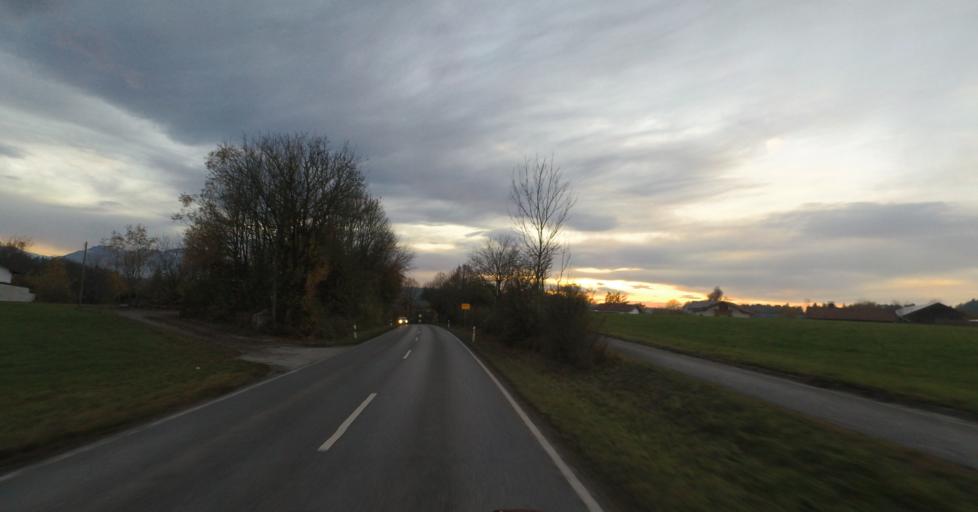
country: DE
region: Bavaria
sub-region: Upper Bavaria
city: Prien am Chiemsee
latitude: 47.8513
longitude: 12.3264
